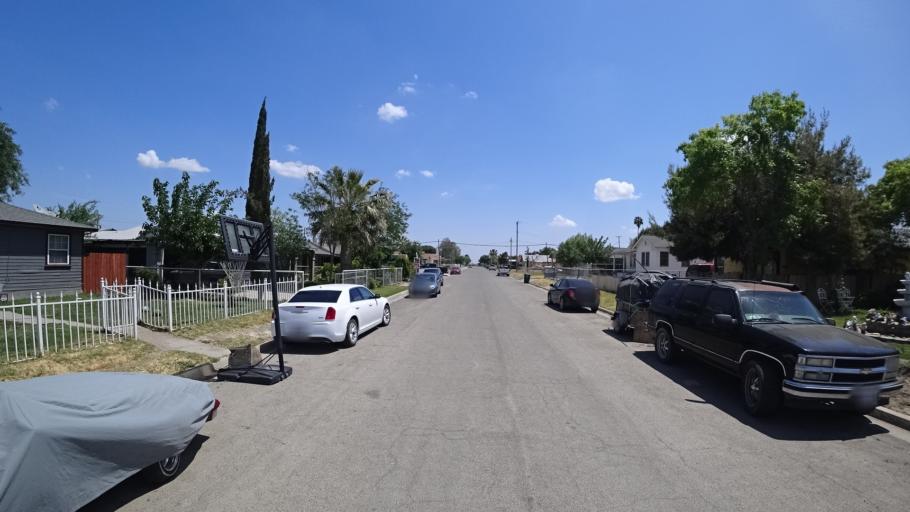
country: US
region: California
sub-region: Kings County
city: Stratford
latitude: 36.1882
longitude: -119.8235
